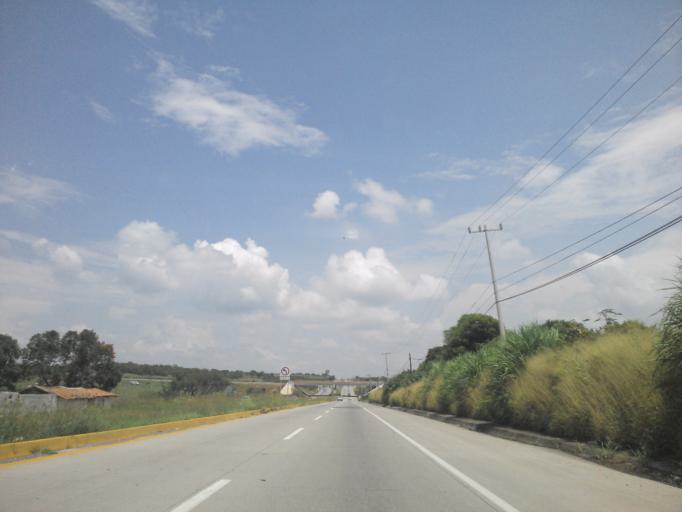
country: MX
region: Jalisco
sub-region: Zapotlanejo
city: La Mezquitera
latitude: 20.5969
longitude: -103.1046
